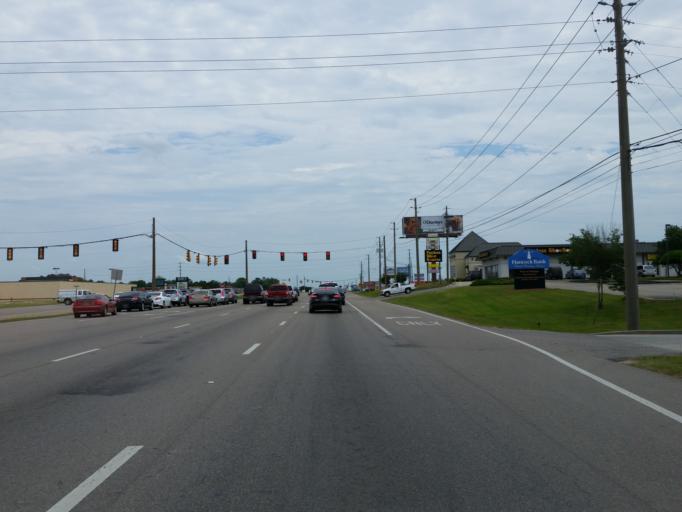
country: US
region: Mississippi
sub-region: Lamar County
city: West Hattiesburg
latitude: 31.3219
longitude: -89.3777
